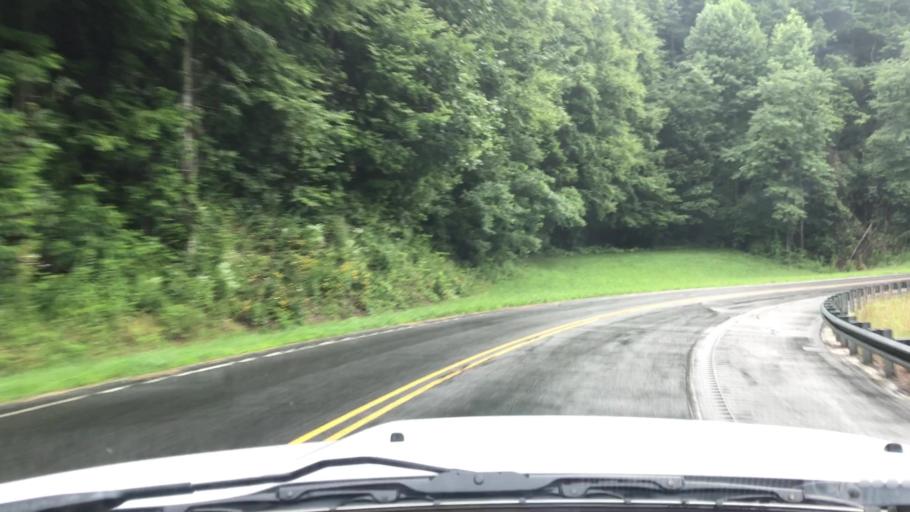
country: US
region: North Carolina
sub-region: Graham County
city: Robbinsville
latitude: 35.2530
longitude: -83.7035
